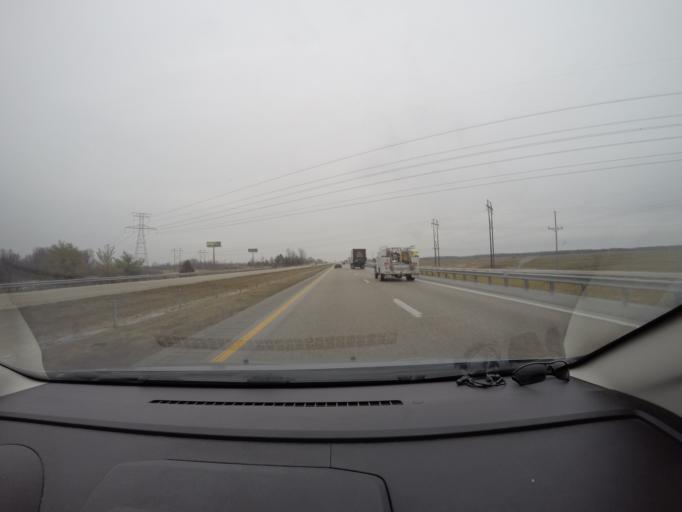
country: US
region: Missouri
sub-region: Montgomery County
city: Montgomery City
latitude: 38.9038
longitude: -91.4875
